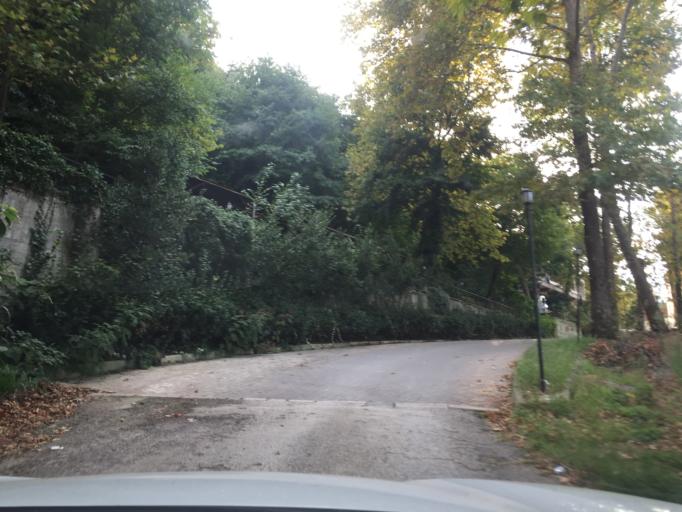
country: TR
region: Balikesir
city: Gonen
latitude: 40.0297
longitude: 27.5635
